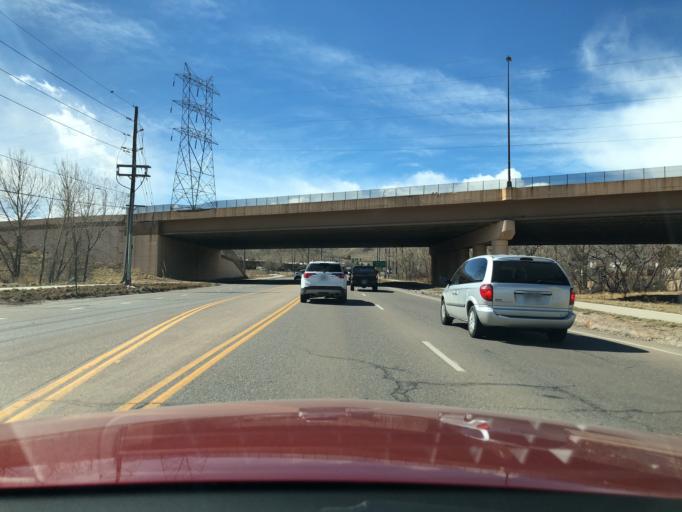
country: US
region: Colorado
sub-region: Jefferson County
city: West Pleasant View
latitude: 39.7216
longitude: -105.1976
